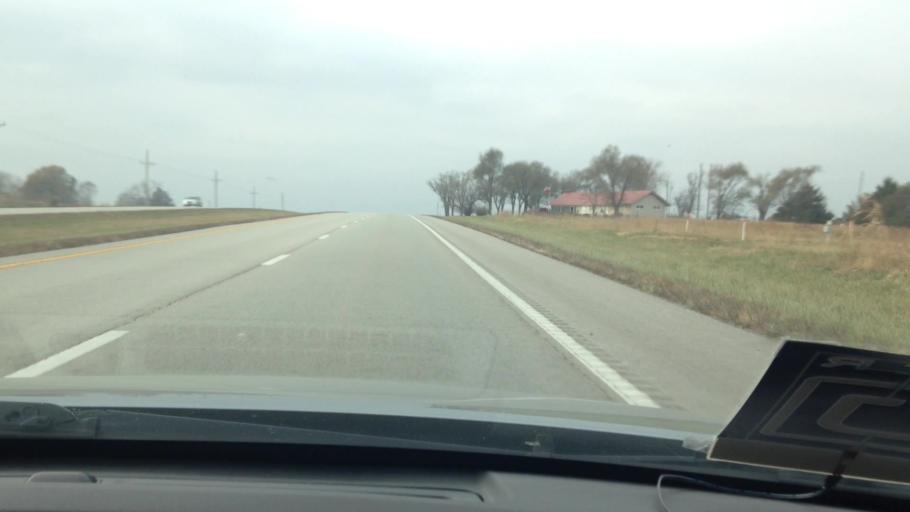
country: US
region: Missouri
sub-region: Cass County
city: Garden City
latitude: 38.5844
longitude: -94.2251
